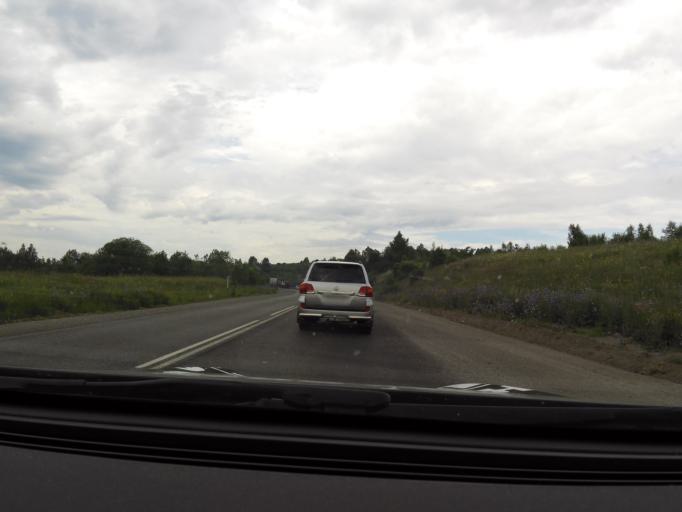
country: RU
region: Chelyabinsk
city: Sim
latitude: 55.0005
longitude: 57.6356
